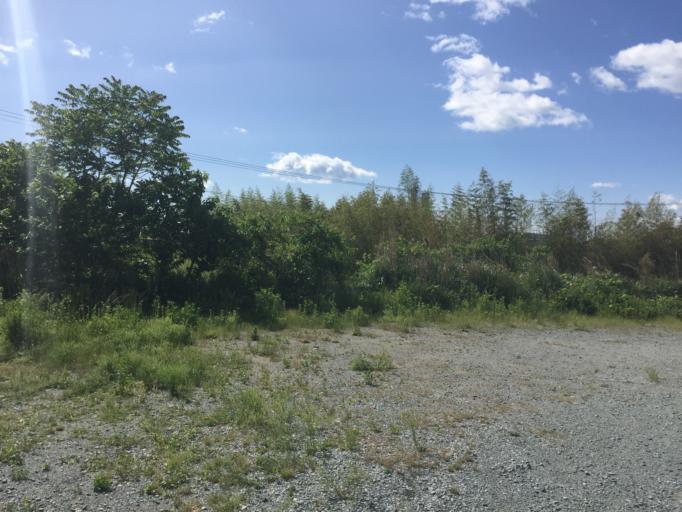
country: JP
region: Fukushima
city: Namie
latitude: 37.4971
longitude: 140.9984
